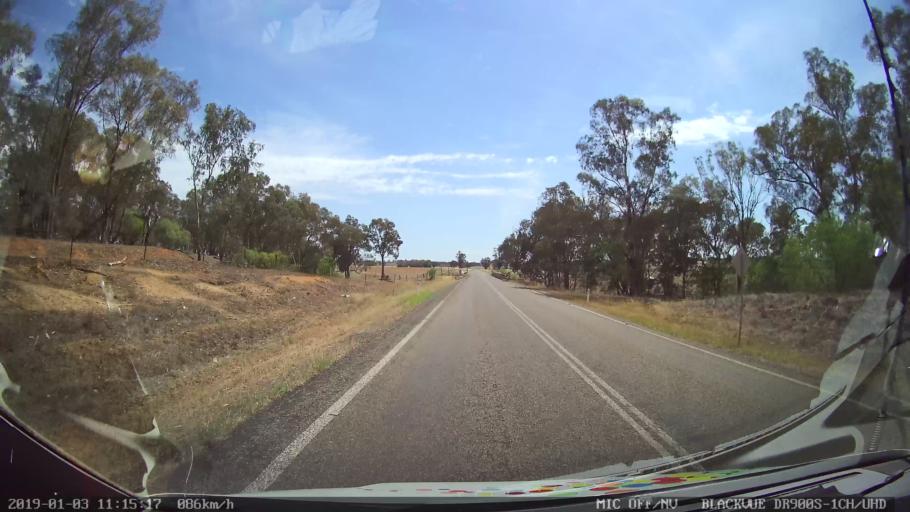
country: AU
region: New South Wales
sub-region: Young
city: Young
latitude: -34.1655
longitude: 148.2634
